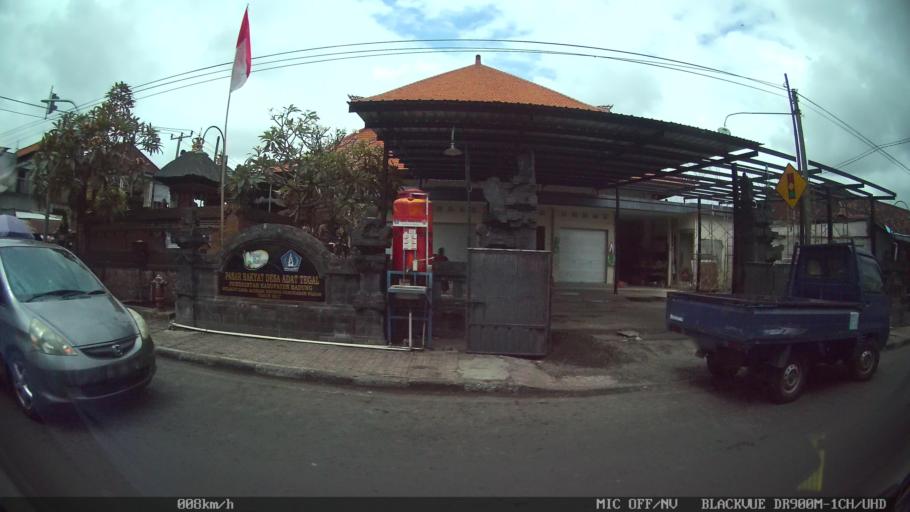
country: ID
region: Bali
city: Banjar Bucu
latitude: -8.5872
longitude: 115.2063
